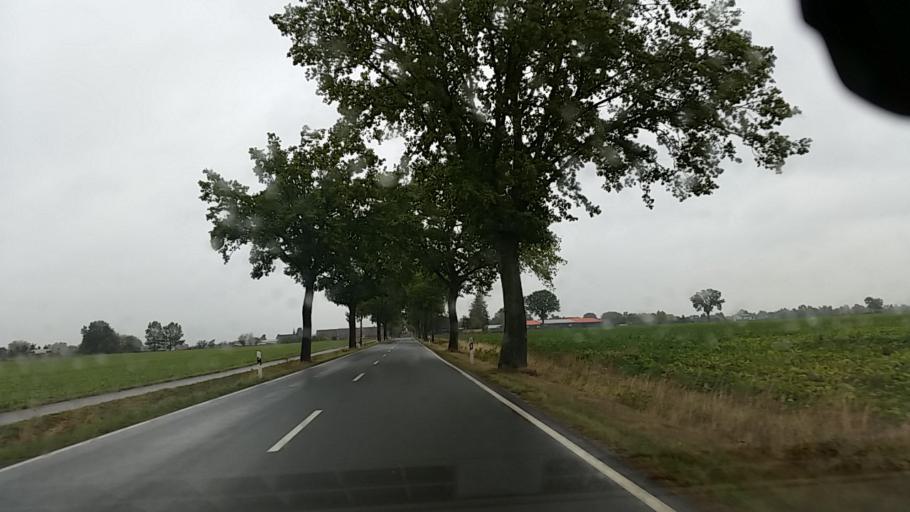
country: DE
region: Lower Saxony
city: Tiddische
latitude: 52.5107
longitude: 10.8043
